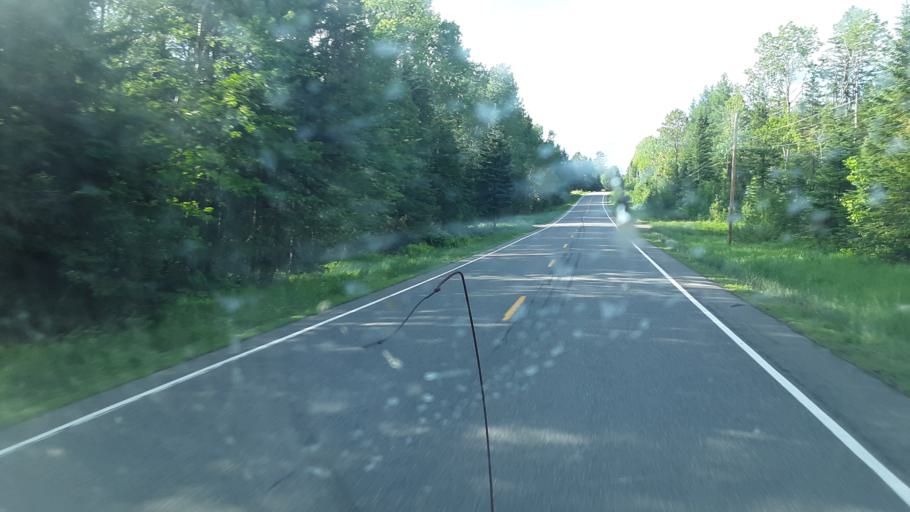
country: US
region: Maine
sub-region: Aroostook County
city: Presque Isle
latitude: 46.4725
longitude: -68.3885
